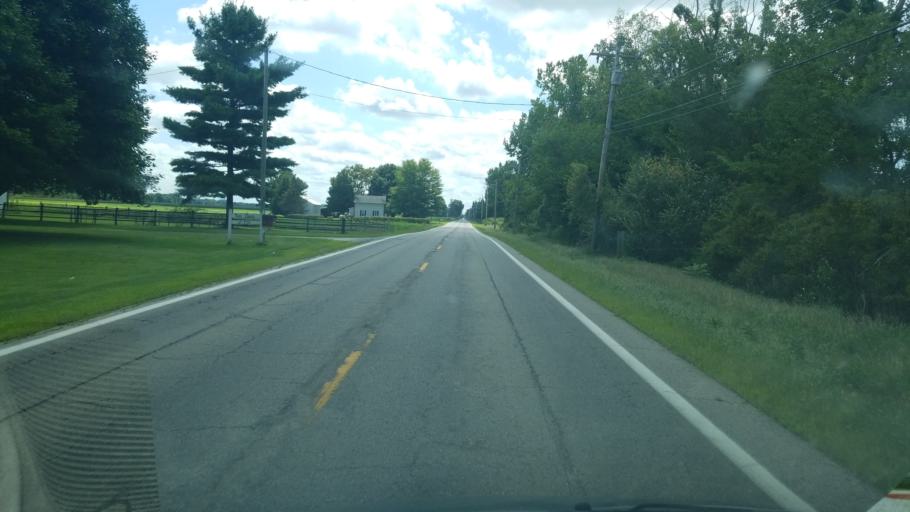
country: US
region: Ohio
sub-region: Henry County
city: Liberty Center
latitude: 41.4838
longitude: -84.0087
